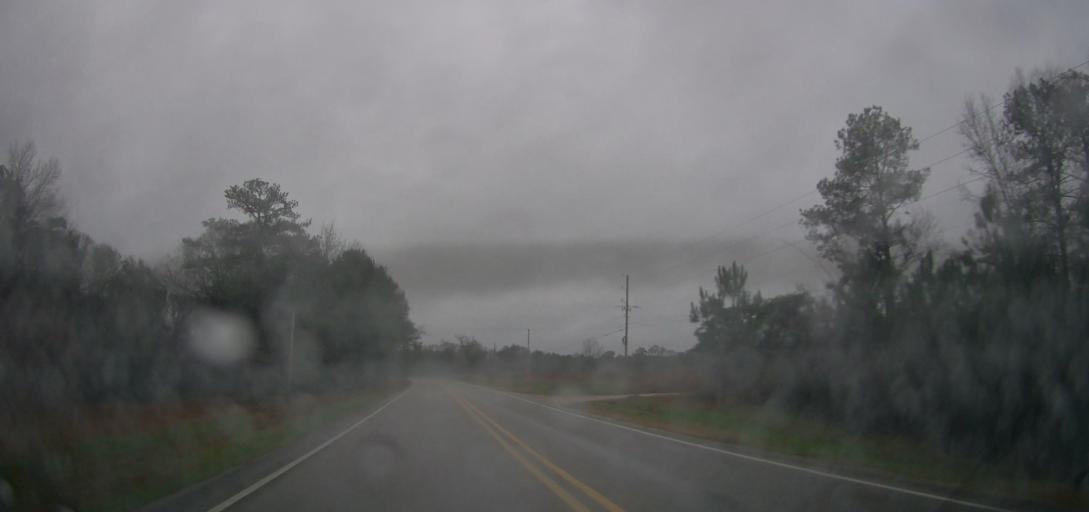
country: US
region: Alabama
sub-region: Autauga County
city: Pine Level
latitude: 32.5362
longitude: -86.6404
